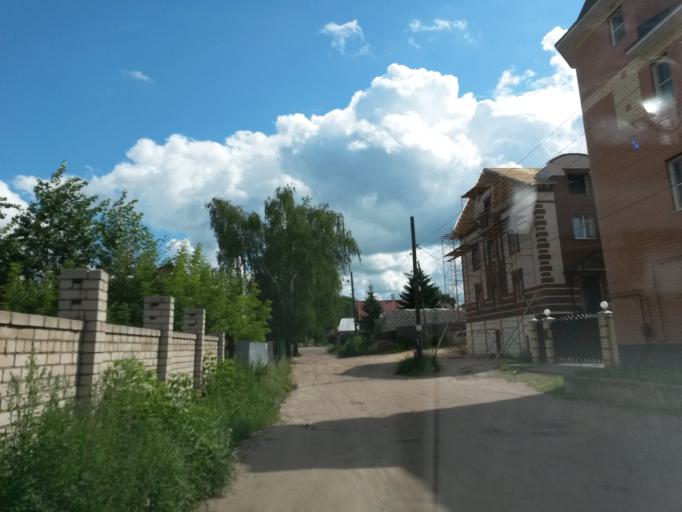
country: RU
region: Jaroslavl
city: Yaroslavl
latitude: 57.6049
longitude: 39.8855
